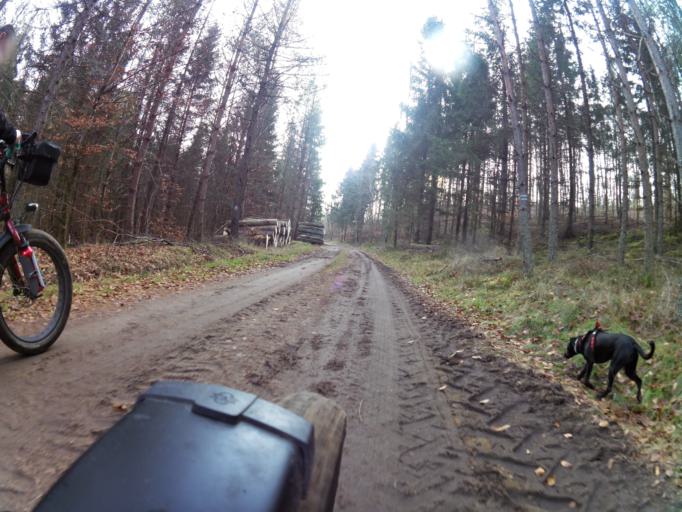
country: PL
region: West Pomeranian Voivodeship
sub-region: Powiat koszalinski
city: Polanow
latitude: 54.1829
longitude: 16.7197
